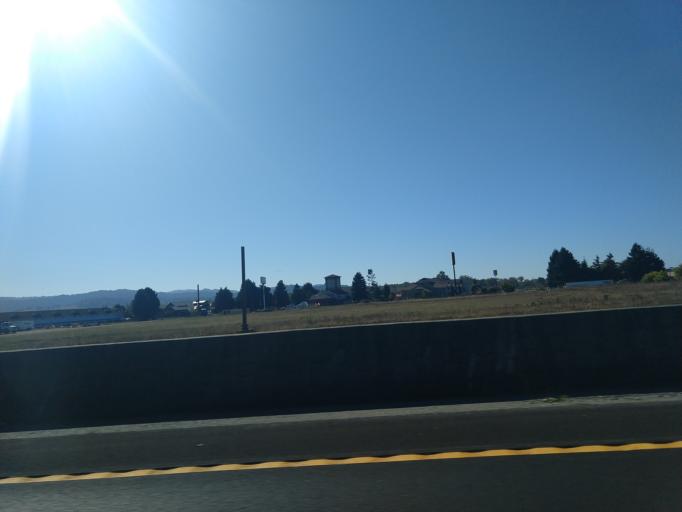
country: US
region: California
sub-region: Humboldt County
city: Fortuna
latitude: 40.5791
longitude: -124.1500
